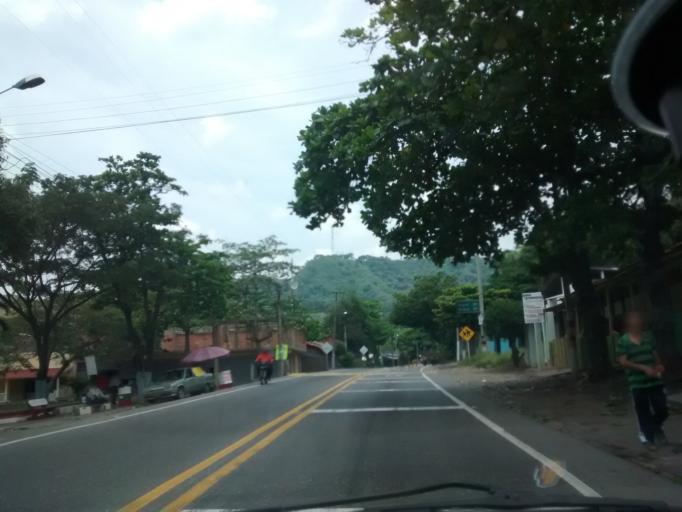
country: CO
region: Tolima
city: Valle de San Juan
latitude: 4.2834
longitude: -75.0313
